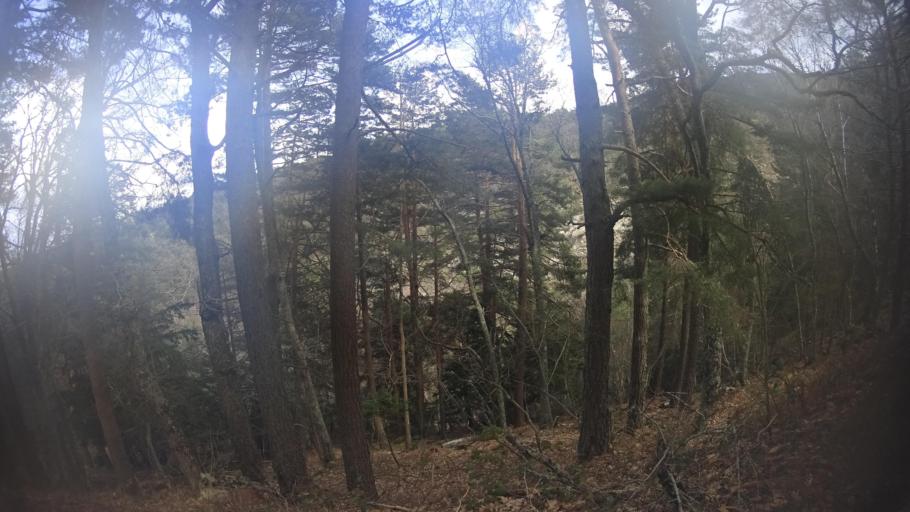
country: ES
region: Madrid
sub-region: Provincia de Madrid
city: Canencia
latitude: 40.8767
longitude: -3.7794
